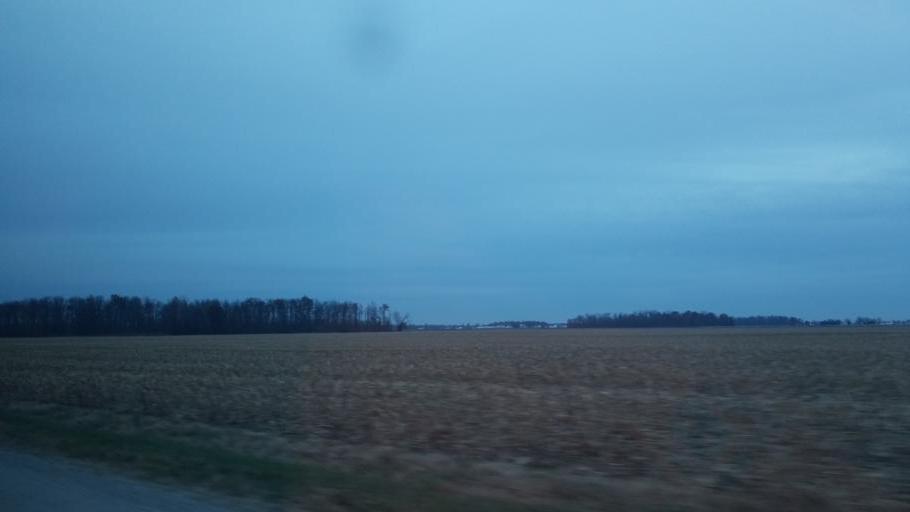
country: US
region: Indiana
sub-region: Adams County
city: Berne
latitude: 40.7456
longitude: -84.9950
